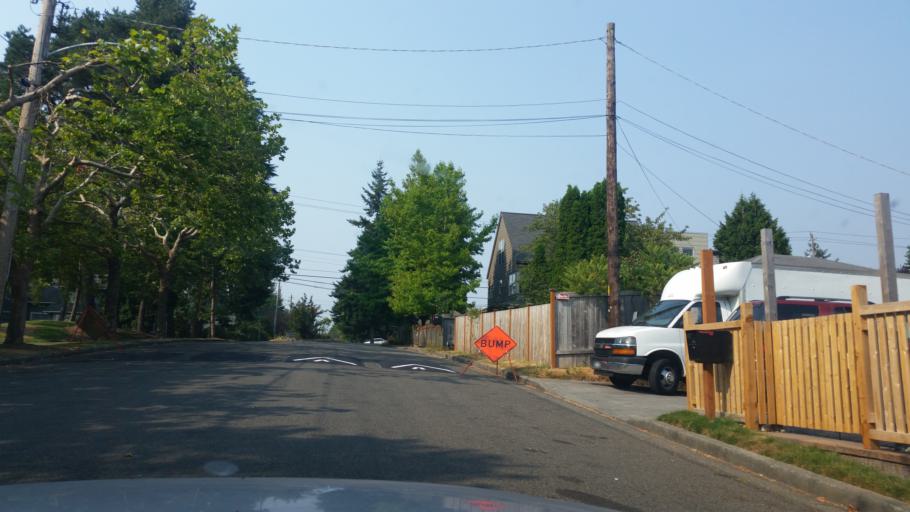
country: US
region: Washington
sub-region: King County
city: Shoreline
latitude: 47.6954
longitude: -122.3581
